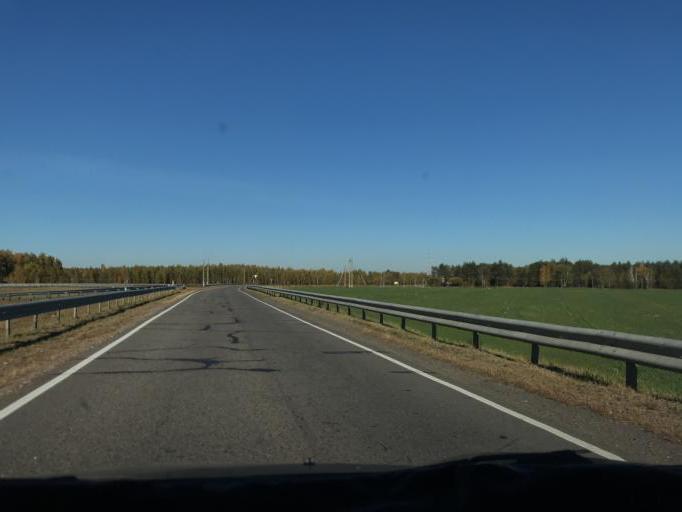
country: BY
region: Gomel
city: Mazyr
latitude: 52.0078
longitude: 29.2571
